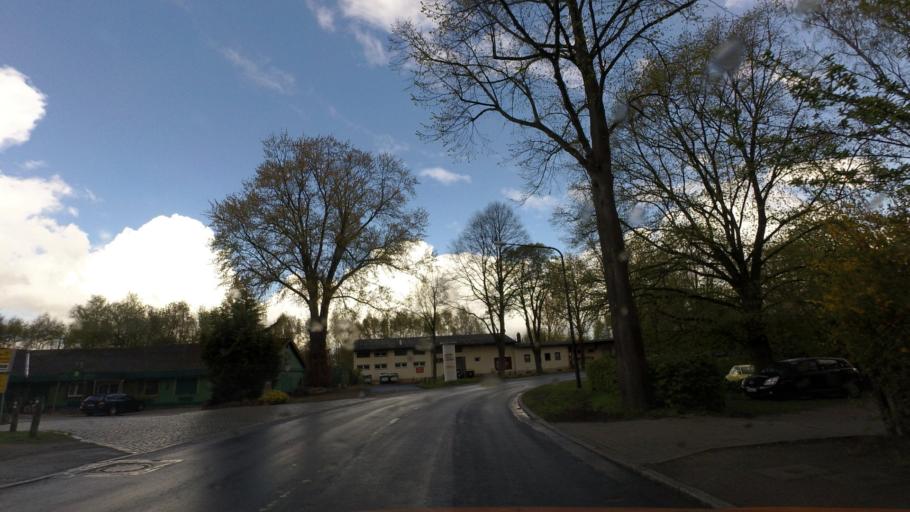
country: DE
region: Lower Saxony
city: Stuhr
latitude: 53.0611
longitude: 8.7366
